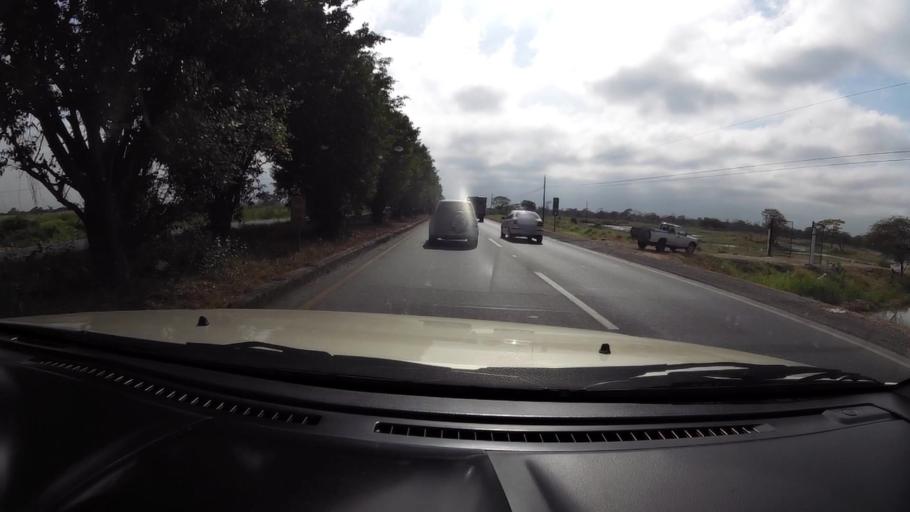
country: EC
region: Guayas
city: Eloy Alfaro
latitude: -2.1991
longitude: -79.7724
